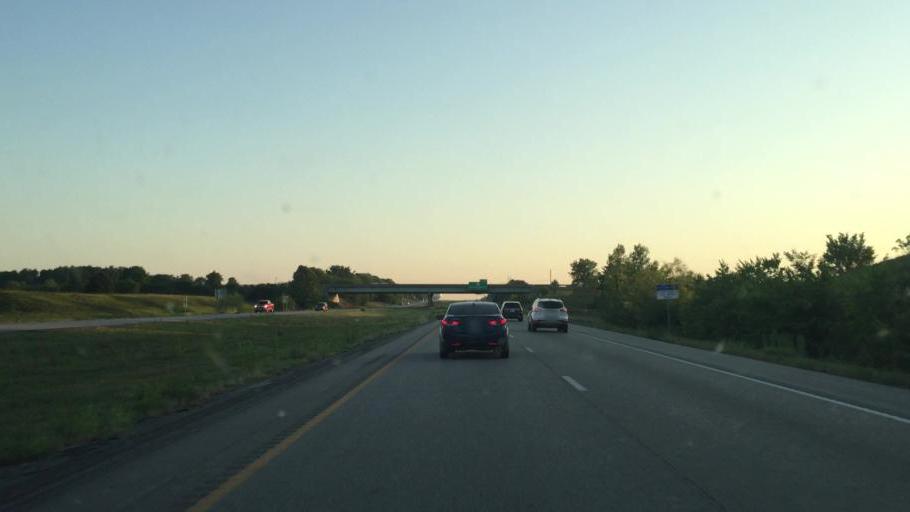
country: US
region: Missouri
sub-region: Clay County
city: Pleasant Valley
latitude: 39.2857
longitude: -94.5101
